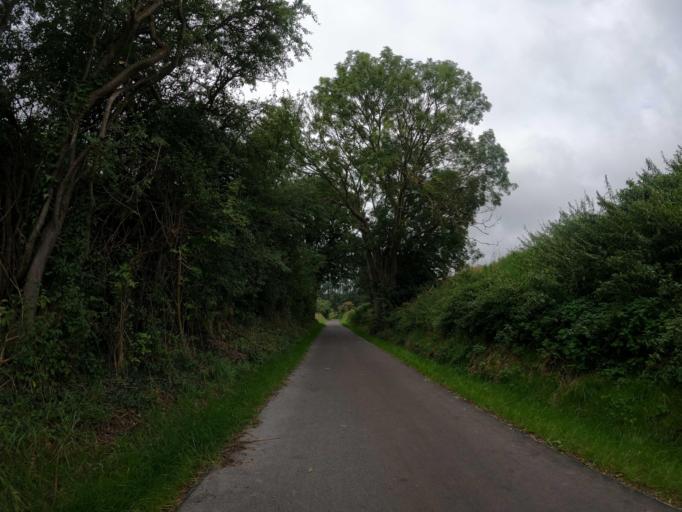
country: DE
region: Mecklenburg-Vorpommern
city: Poseritz
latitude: 54.2961
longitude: 13.2146
